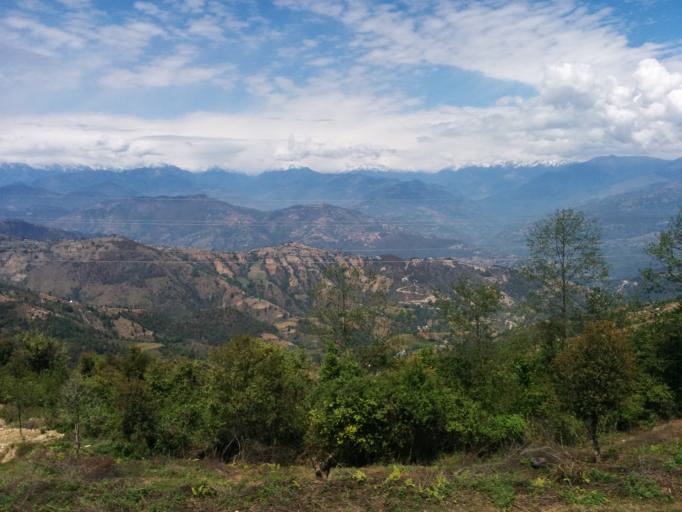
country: NP
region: Central Region
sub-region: Bagmati Zone
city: Nagarkot
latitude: 27.7285
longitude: 85.5237
